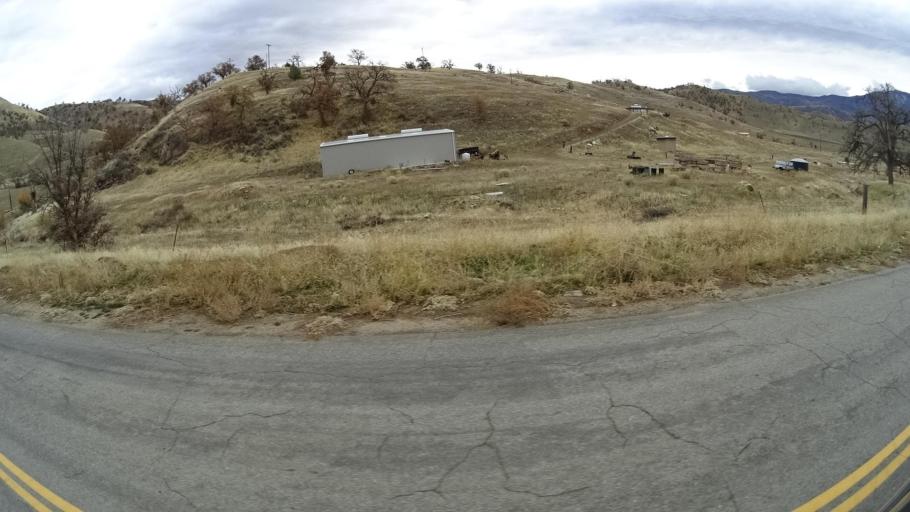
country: US
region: California
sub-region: Kern County
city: Bear Valley Springs
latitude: 35.1338
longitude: -118.5637
